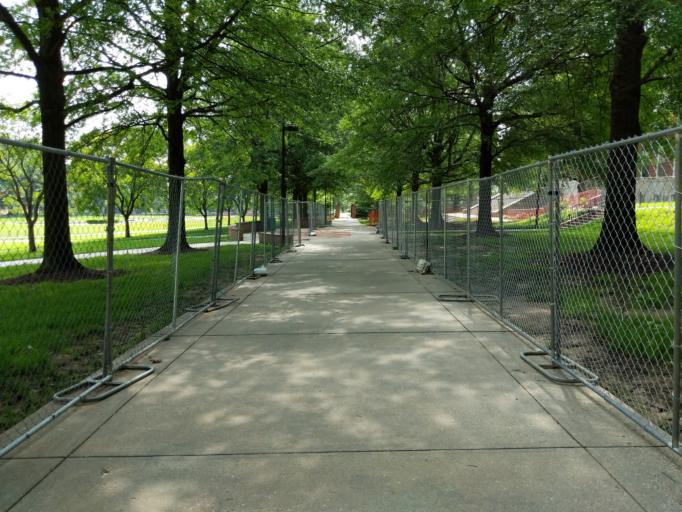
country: US
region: Maryland
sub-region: Prince George's County
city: College Park
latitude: 38.9854
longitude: -76.9440
